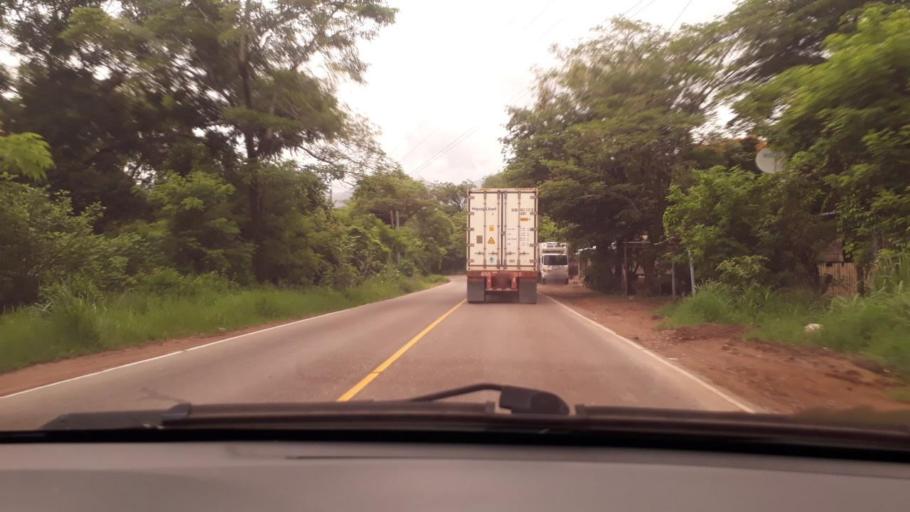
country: GT
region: Chiquimula
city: Quezaltepeque
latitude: 14.6132
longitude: -89.4517
